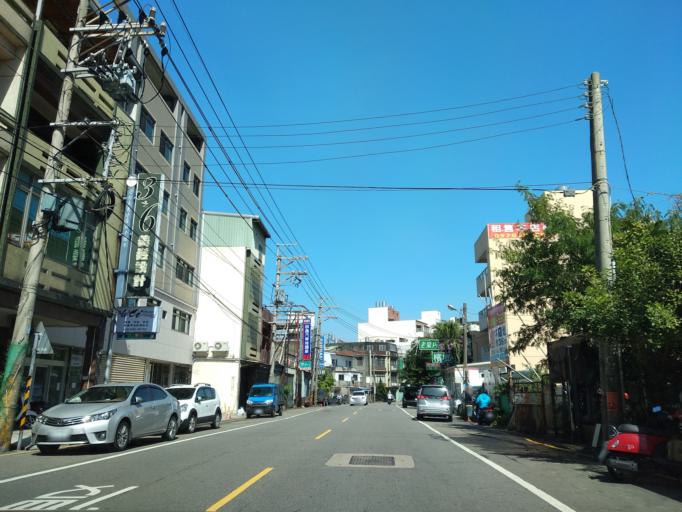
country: TW
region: Taiwan
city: Taoyuan City
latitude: 24.9481
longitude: 121.2212
